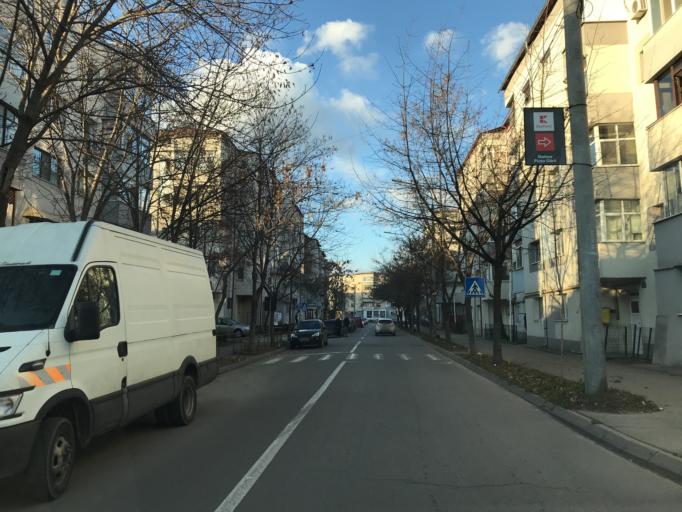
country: RO
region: Olt
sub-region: Municipiul Slatina
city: Slatina
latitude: 44.4218
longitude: 24.3817
